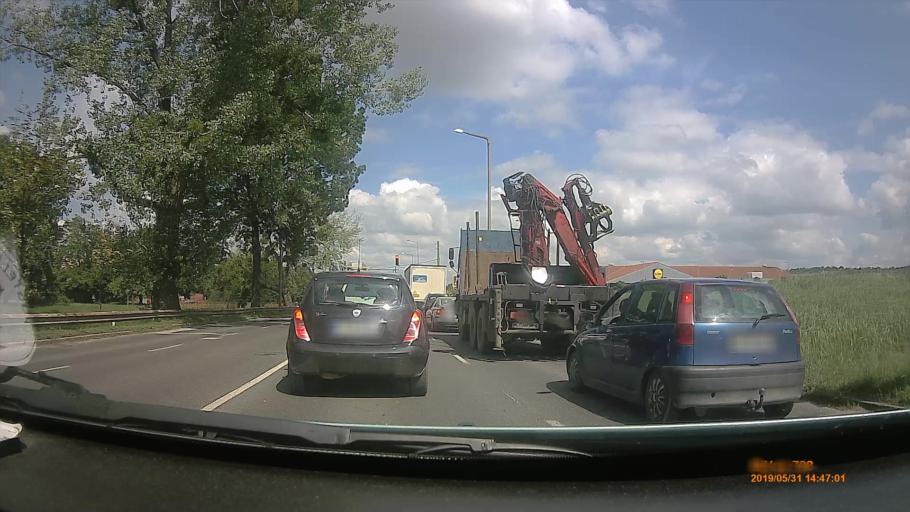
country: HU
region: Borsod-Abauj-Zemplen
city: Sajobabony
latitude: 48.1308
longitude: 20.7109
